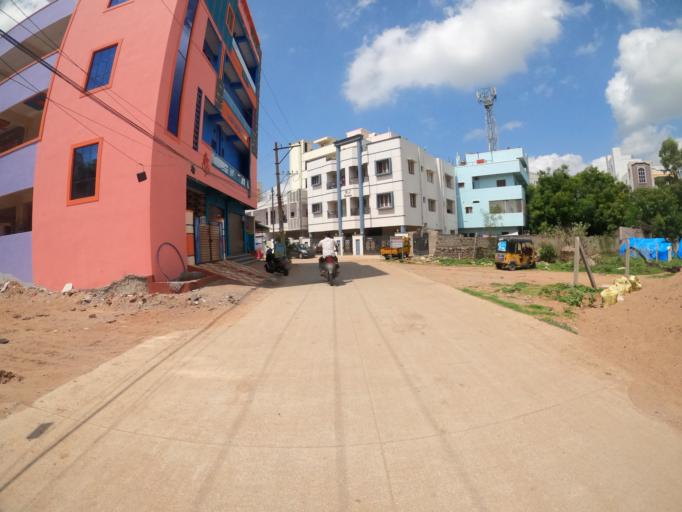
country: IN
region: Telangana
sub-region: Hyderabad
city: Hyderabad
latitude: 17.3619
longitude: 78.3862
